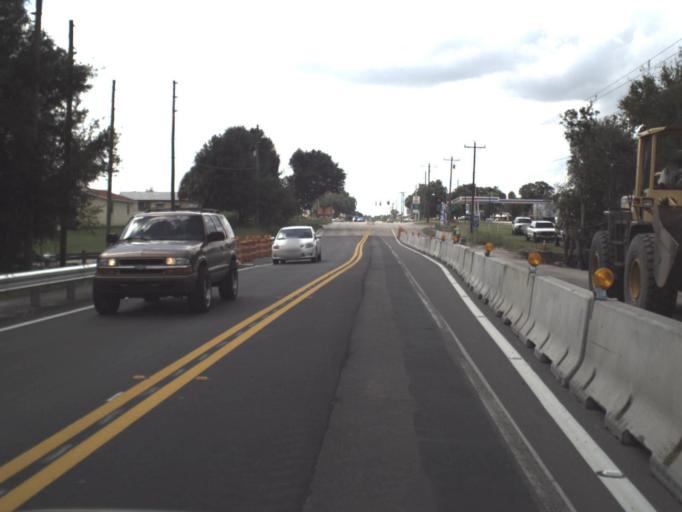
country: US
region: Florida
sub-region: Hardee County
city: Zolfo Springs
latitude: 27.5002
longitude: -81.7947
